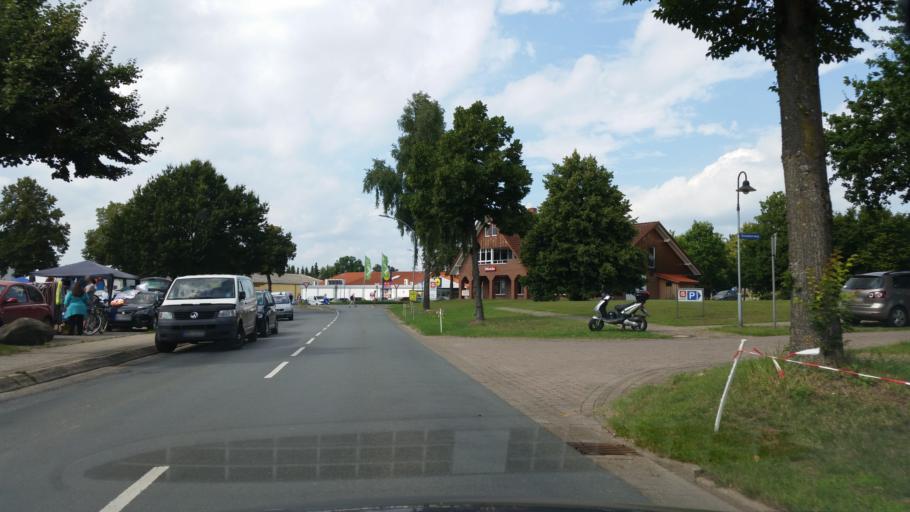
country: DE
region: Lower Saxony
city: Neuenkirchen
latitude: 53.0383
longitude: 9.7097
